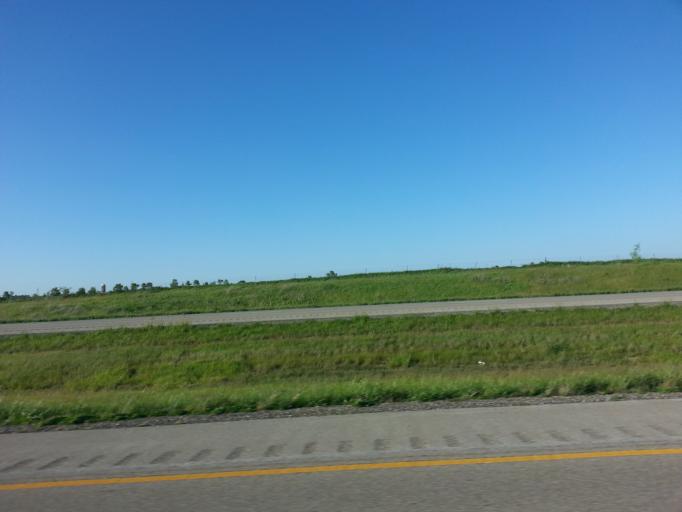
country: US
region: Illinois
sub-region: McLean County
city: Le Roy
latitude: 40.3495
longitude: -88.7885
